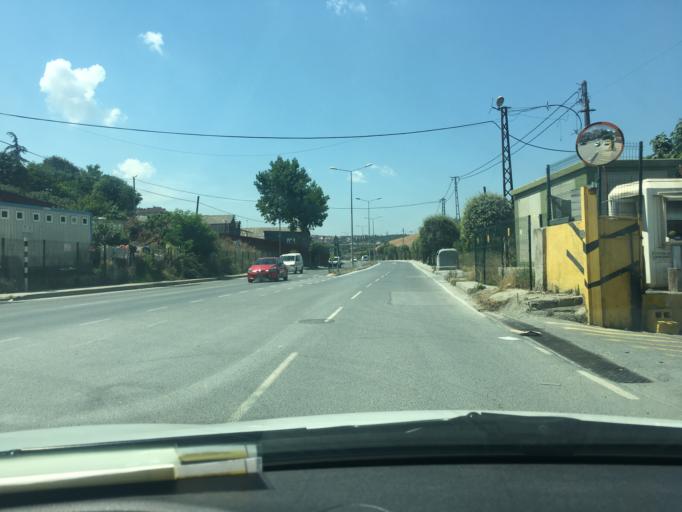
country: TR
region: Istanbul
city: Sisli
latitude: 41.0878
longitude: 28.9351
